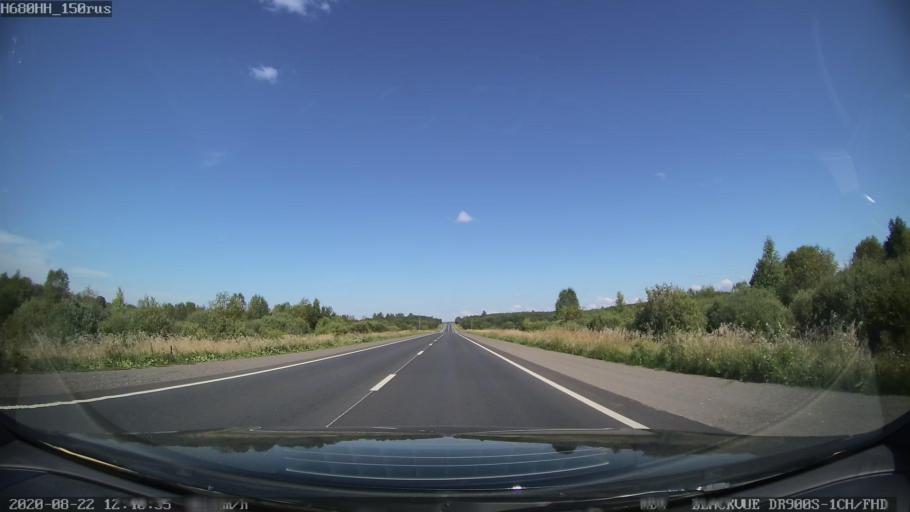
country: RU
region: Tverskaya
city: Rameshki
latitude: 57.3361
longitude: 36.0949
